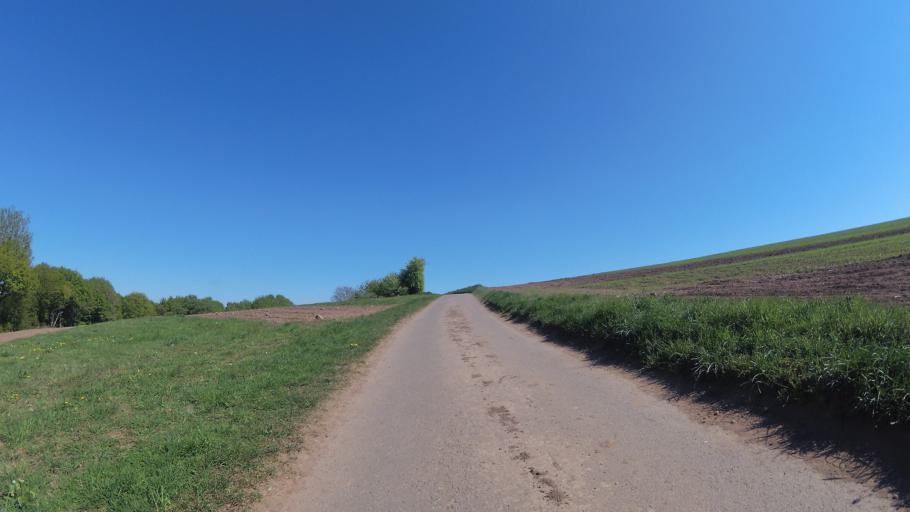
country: DE
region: Saarland
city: Hangard
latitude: 49.3903
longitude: 7.2026
